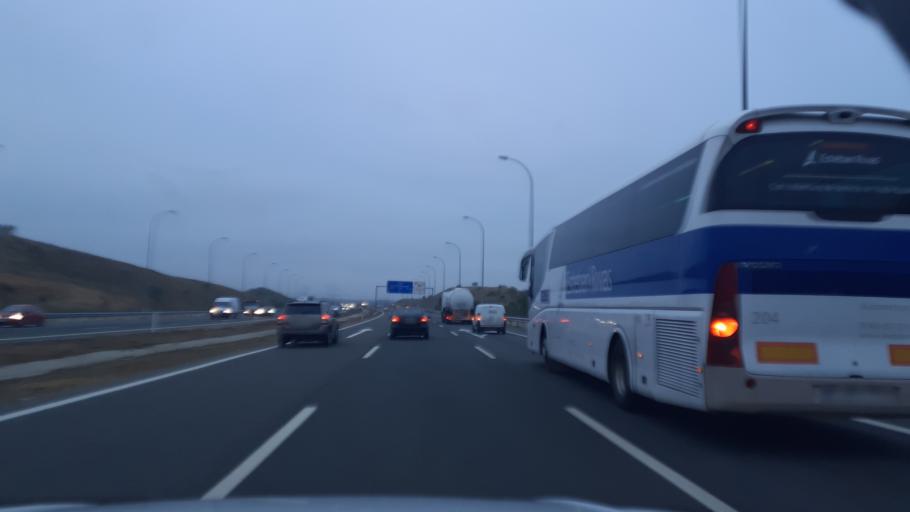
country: ES
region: Madrid
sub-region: Provincia de Madrid
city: Paracuellos de Jarama
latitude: 40.4881
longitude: -3.4967
